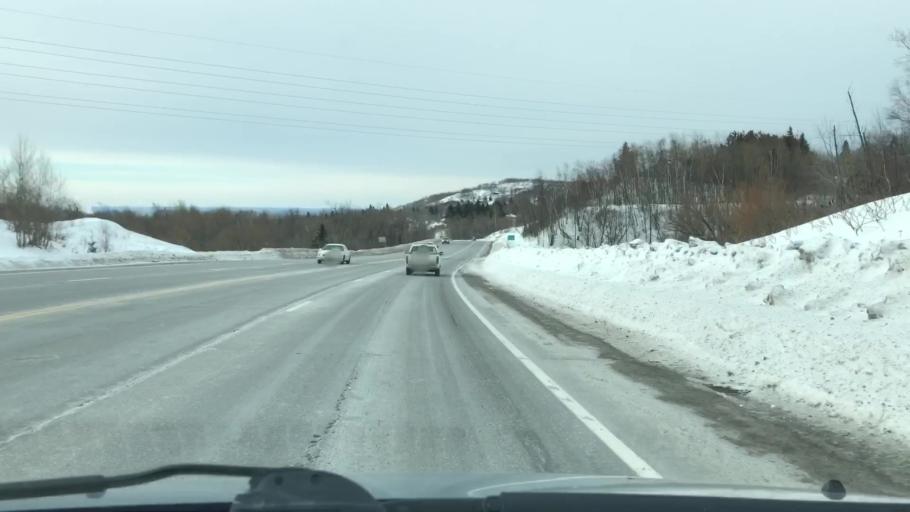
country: US
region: Minnesota
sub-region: Saint Louis County
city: Duluth
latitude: 46.7789
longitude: -92.1402
